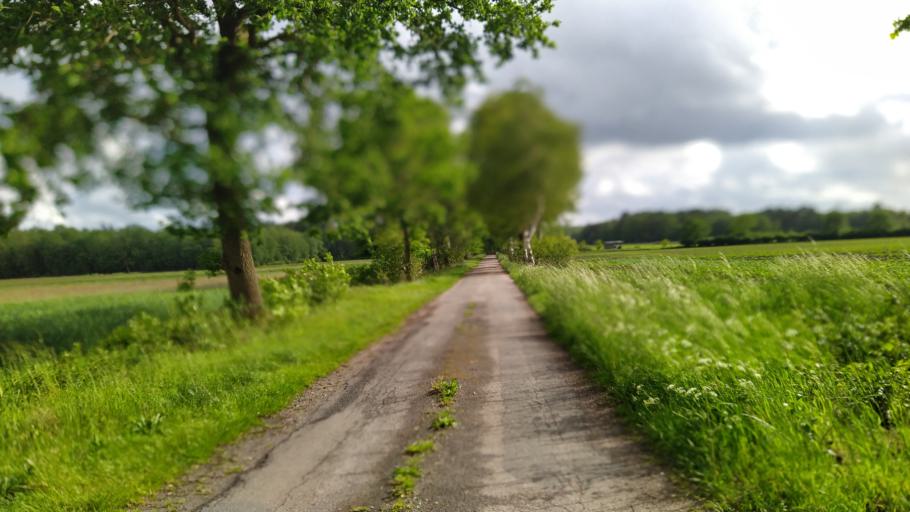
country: DE
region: Lower Saxony
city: Farven
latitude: 53.4248
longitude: 9.3519
